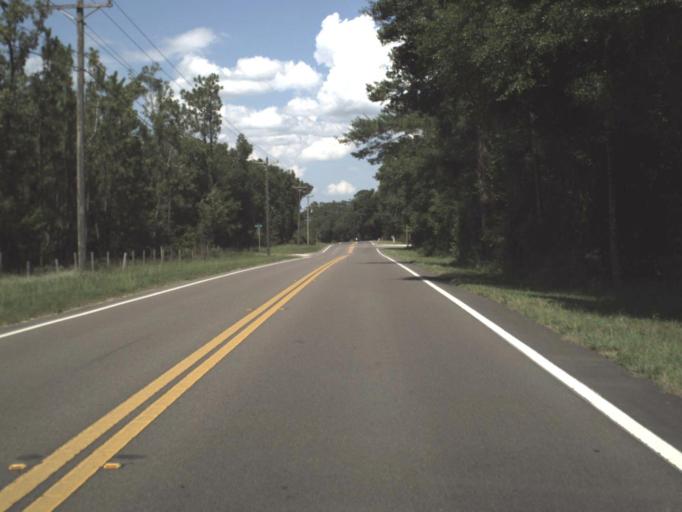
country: US
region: Florida
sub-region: Clay County
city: Keystone Heights
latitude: 29.7155
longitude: -82.0144
